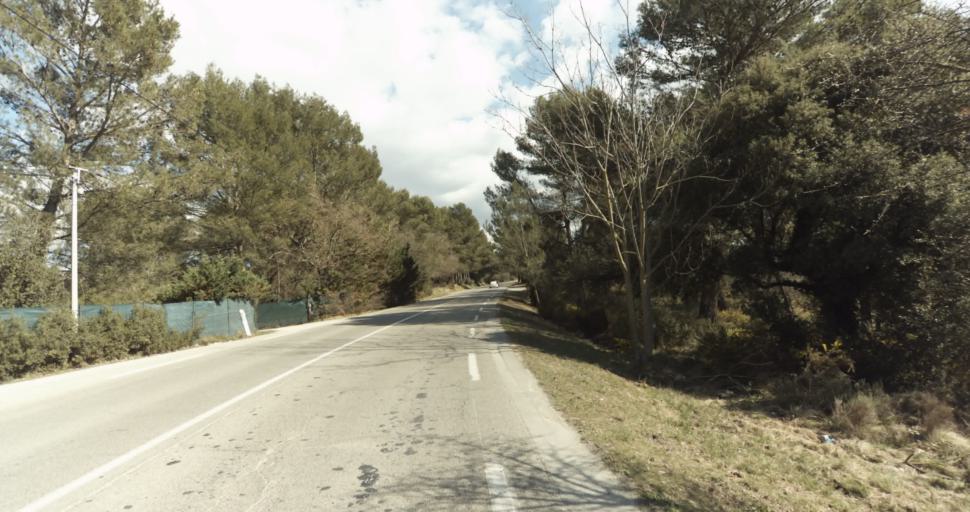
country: FR
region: Provence-Alpes-Cote d'Azur
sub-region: Departement des Bouches-du-Rhone
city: Mimet
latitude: 43.4494
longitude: 5.5088
